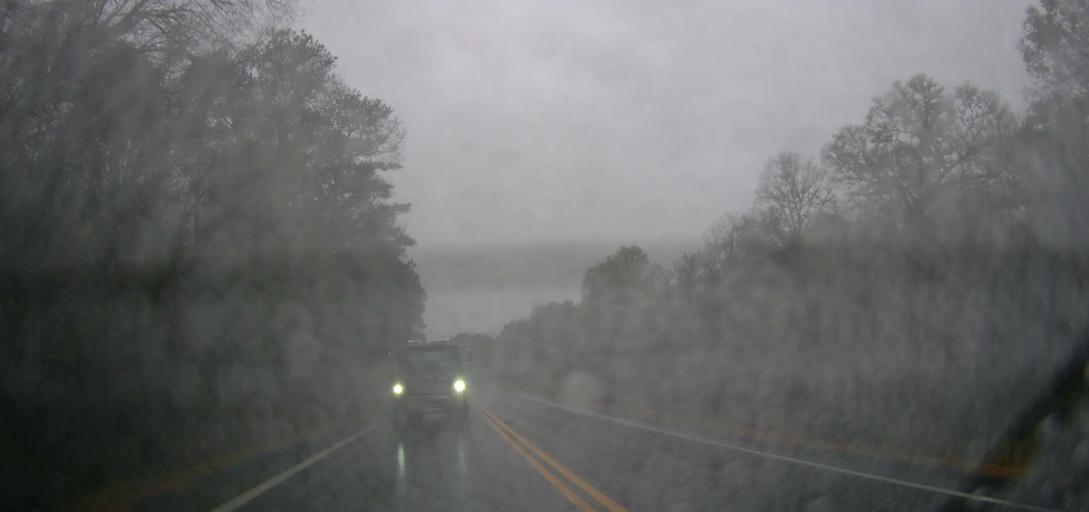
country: US
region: Georgia
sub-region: Putnam County
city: Eatonton
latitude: 33.1882
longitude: -83.4350
